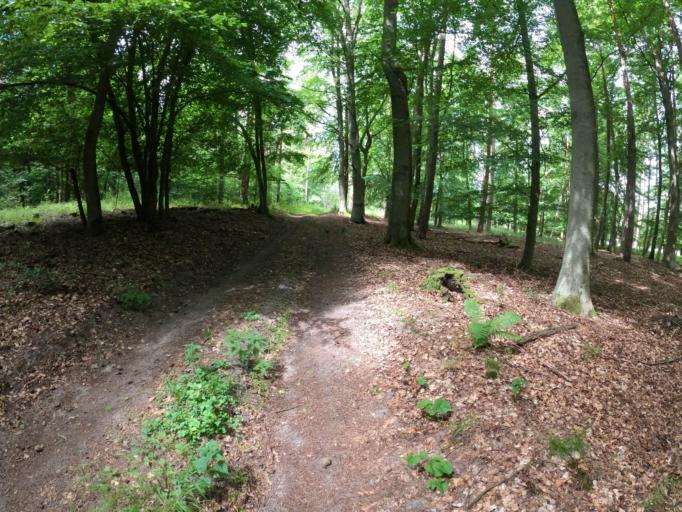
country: DE
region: Brandenburg
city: Angermunde
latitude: 53.0366
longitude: 13.9346
